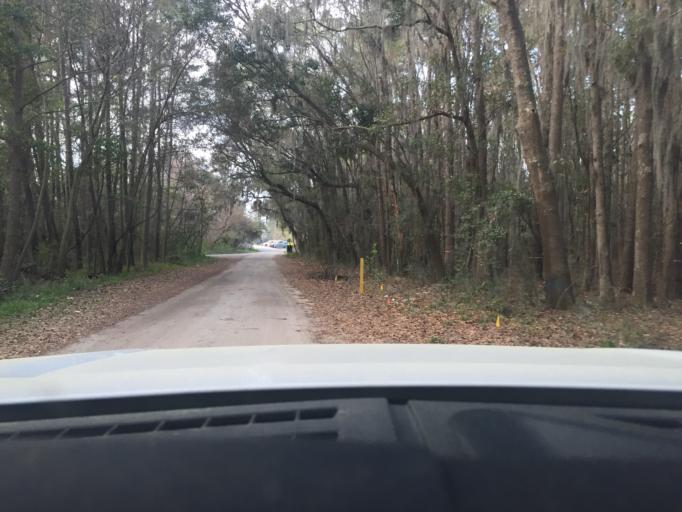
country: US
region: Georgia
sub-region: Chatham County
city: Isle of Hope
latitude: 32.0102
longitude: -81.0907
